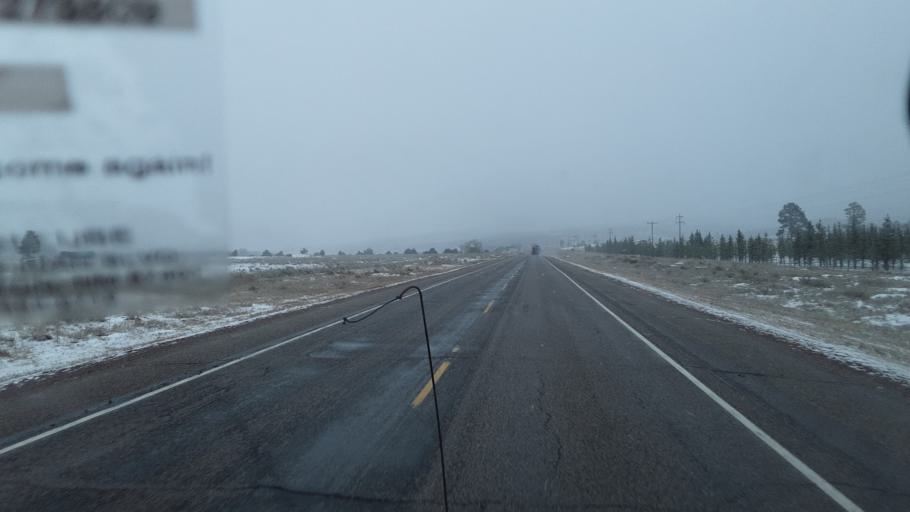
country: US
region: New Mexico
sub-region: Rio Arriba County
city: Tierra Amarilla
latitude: 36.7674
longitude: -106.5567
